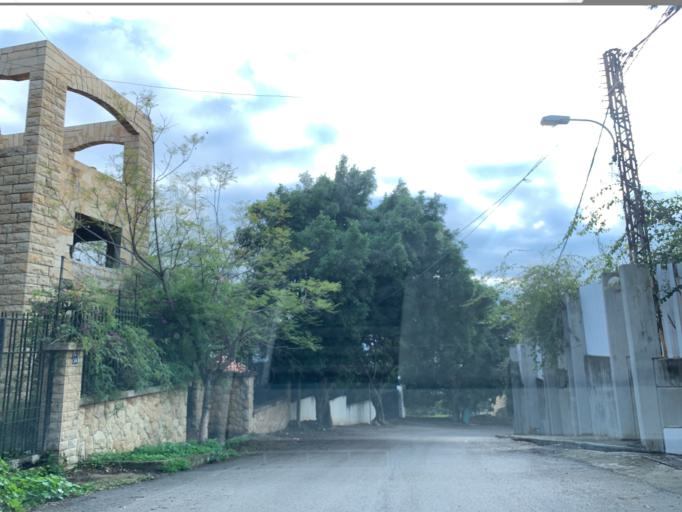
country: LB
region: Mont-Liban
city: Baabda
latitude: 33.8511
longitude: 35.5790
